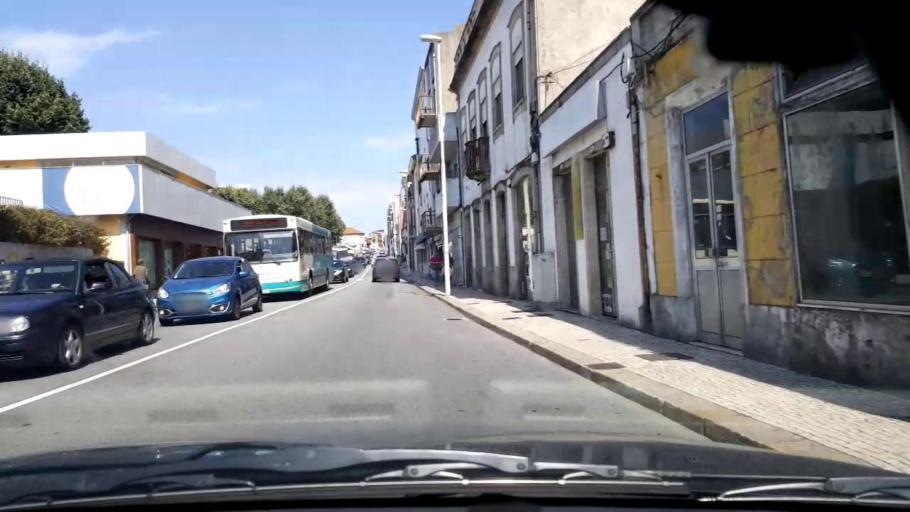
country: PT
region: Porto
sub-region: Vila do Conde
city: Vila do Conde
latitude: 41.3537
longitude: -8.7410
